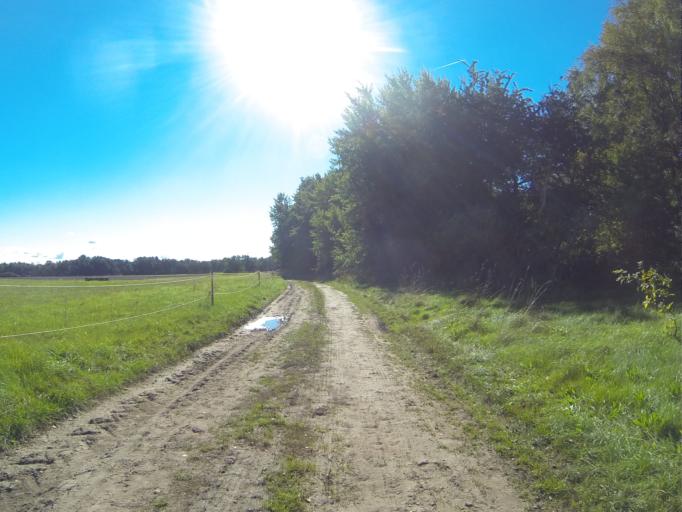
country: SE
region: Skane
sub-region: Hoors Kommun
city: Loberod
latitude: 55.7285
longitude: 13.4097
